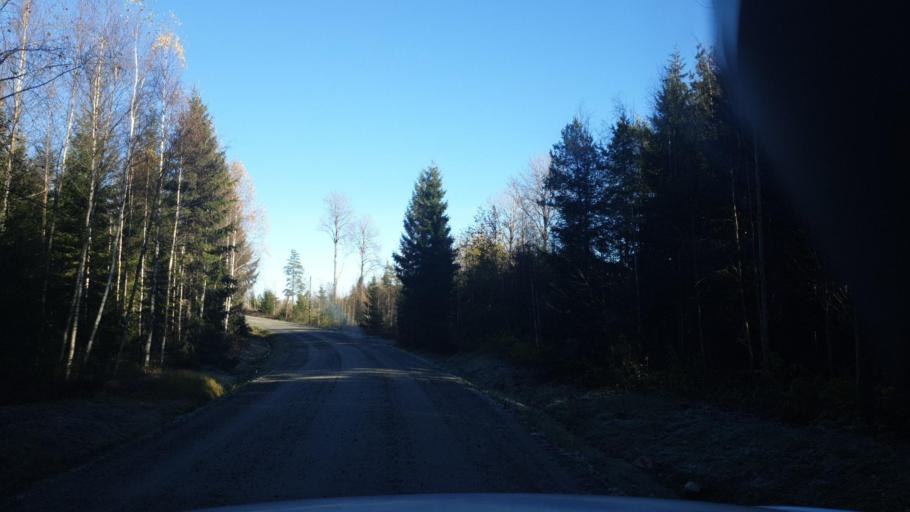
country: SE
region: Vaermland
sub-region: Karlstads Kommun
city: Edsvalla
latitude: 59.5061
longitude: 13.2053
